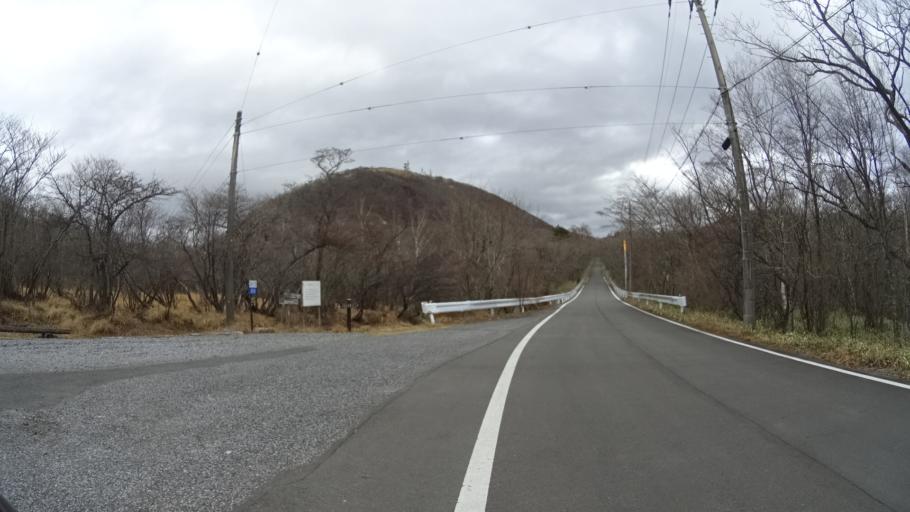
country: JP
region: Gunma
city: Omamacho-omama
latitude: 36.5303
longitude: 139.1720
